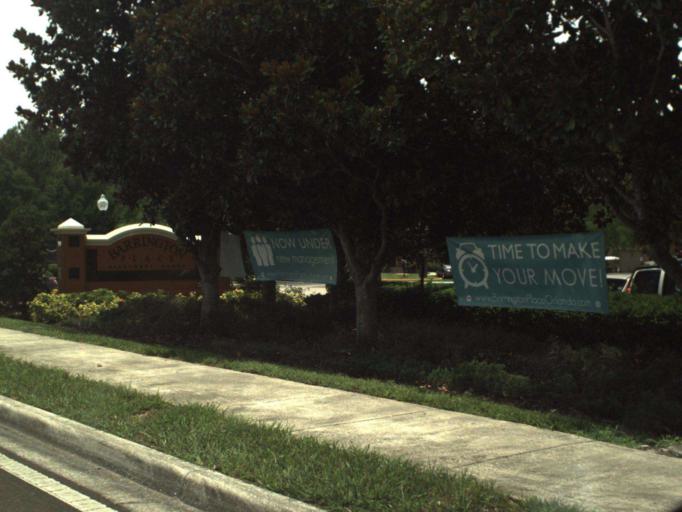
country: US
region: Florida
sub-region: Seminole County
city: Goldenrod
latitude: 28.6199
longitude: -81.2490
